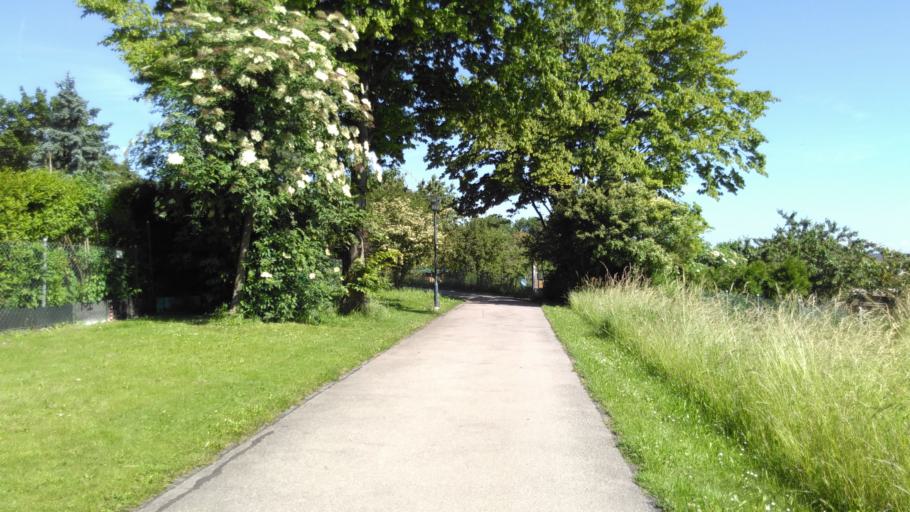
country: CH
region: Zurich
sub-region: Bezirk Zuerich
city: Zuerich (Kreis 3)
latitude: 47.3537
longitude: 8.5060
